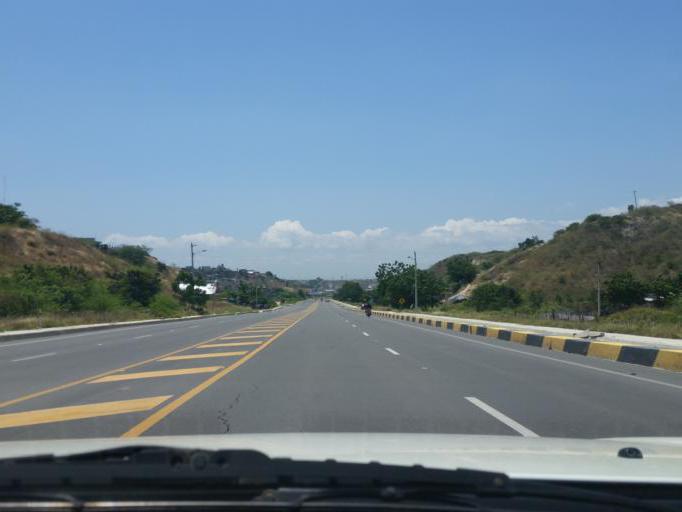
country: EC
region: Manabi
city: Manta
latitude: -0.9612
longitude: -80.7476
